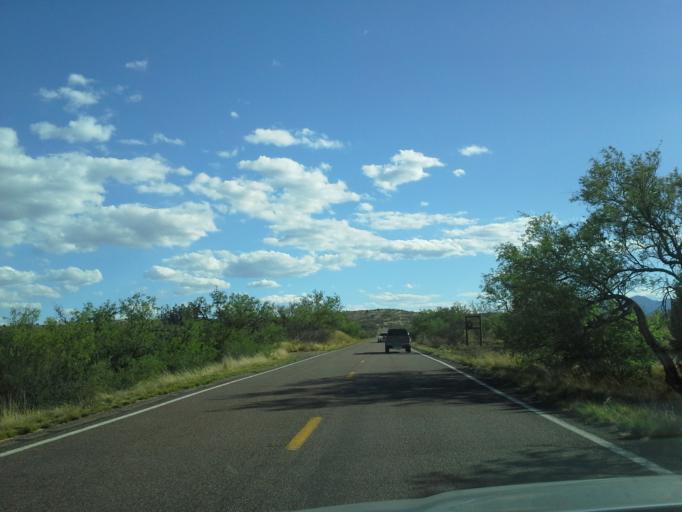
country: US
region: Arizona
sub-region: Pima County
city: Corona de Tucson
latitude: 31.8555
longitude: -110.6953
